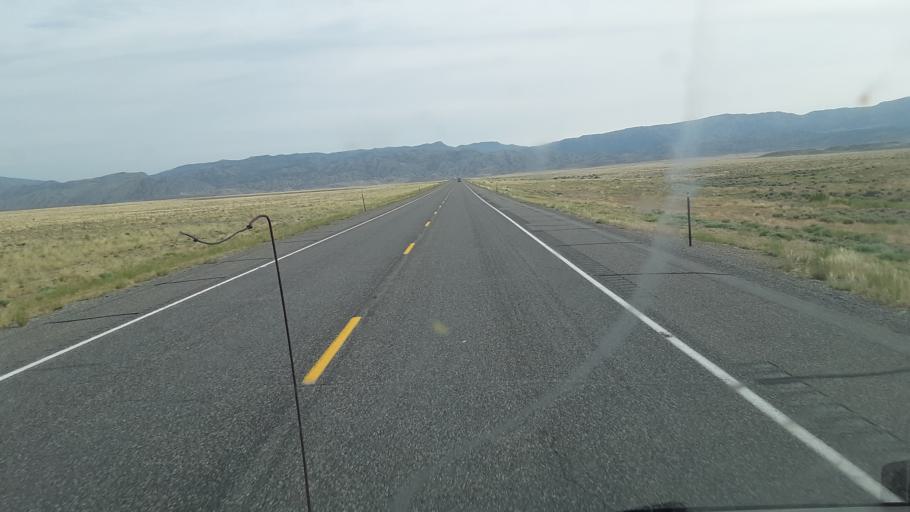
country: US
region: Wyoming
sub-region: Hot Springs County
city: Thermopolis
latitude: 43.3352
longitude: -108.1210
